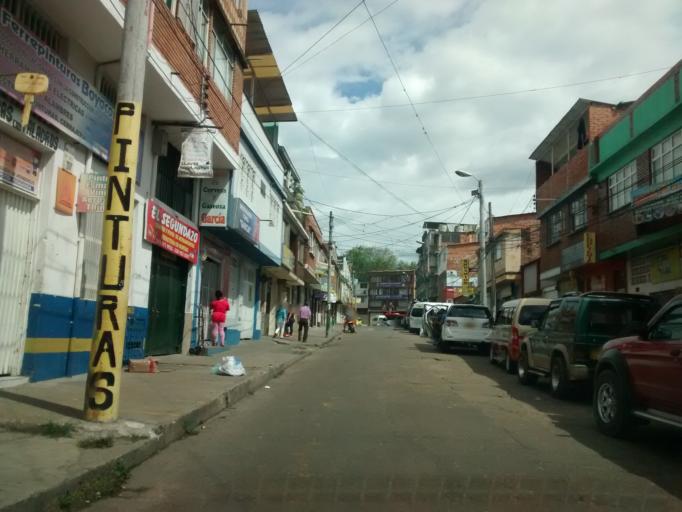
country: CO
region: Cundinamarca
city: Fusagasuga
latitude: 4.3412
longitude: -74.3652
